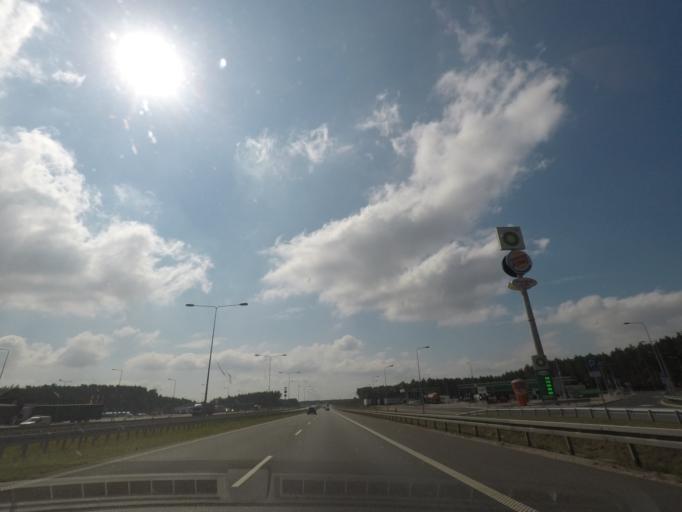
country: PL
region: Kujawsko-Pomorskie
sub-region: Powiat aleksandrowski
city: Aleksandrow Kujawski
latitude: 52.9028
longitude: 18.7217
